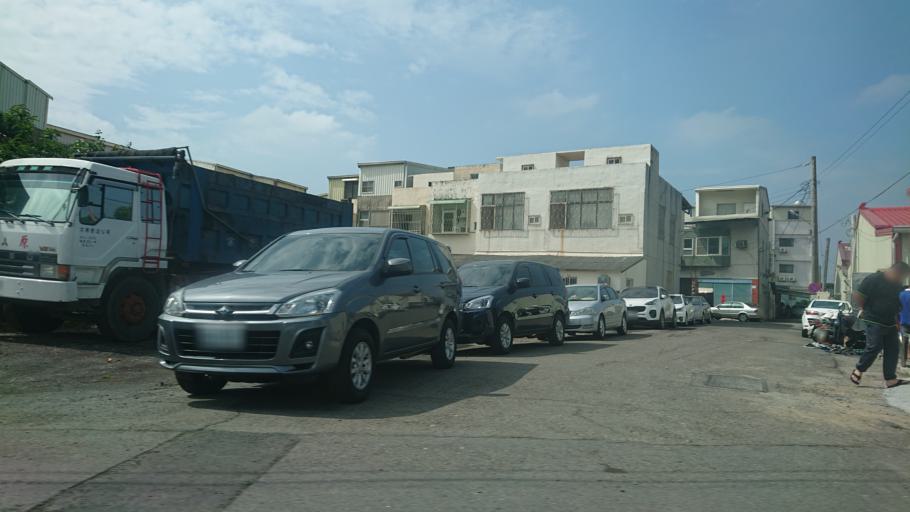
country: TW
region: Taiwan
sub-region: Chiayi
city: Taibao
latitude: 23.4713
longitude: 120.2445
